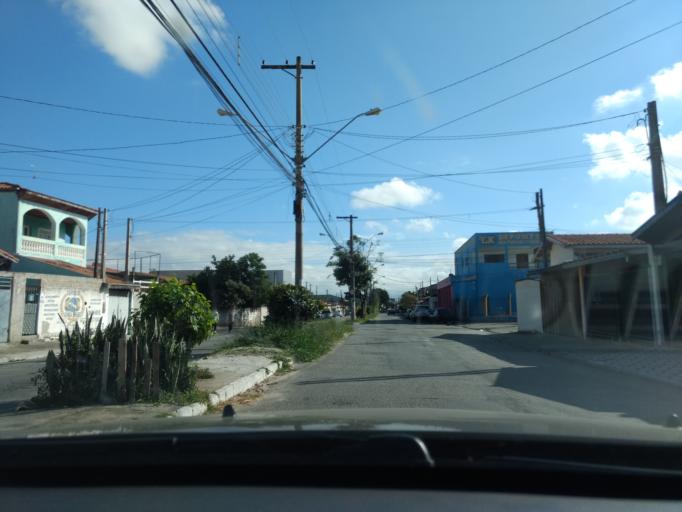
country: BR
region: Sao Paulo
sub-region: Taubate
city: Taubate
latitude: -23.0065
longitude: -45.5272
